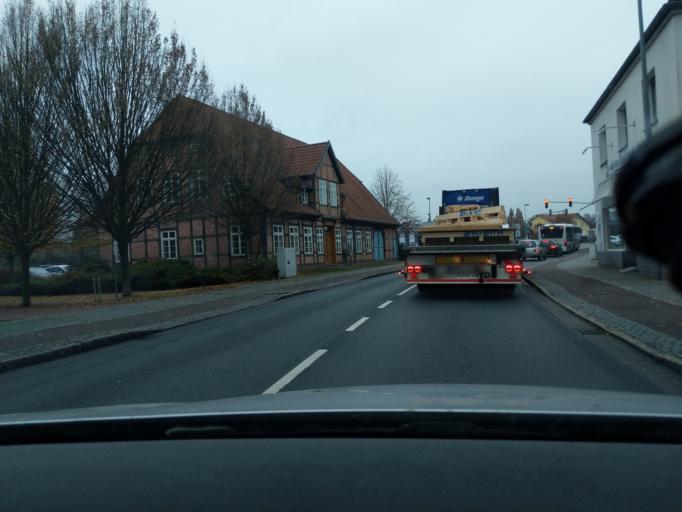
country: DE
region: Lower Saxony
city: Zeven
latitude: 53.2953
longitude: 9.2770
